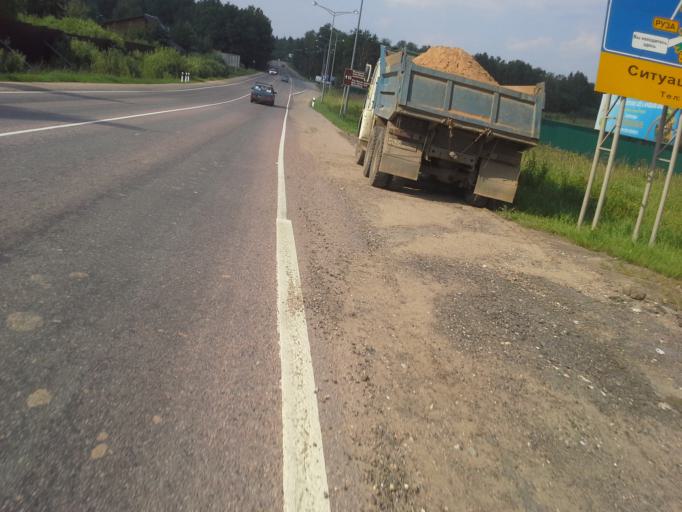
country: RU
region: Moskovskaya
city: Istra
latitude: 55.8613
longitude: 36.7982
